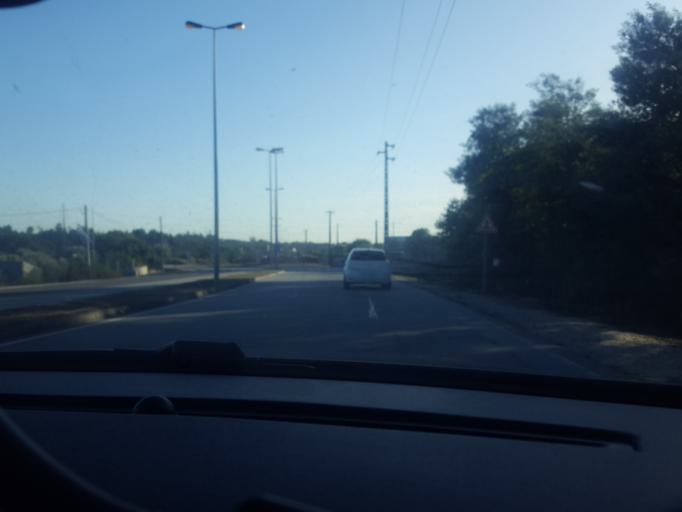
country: PT
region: Viseu
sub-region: Nelas
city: Nelas
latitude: 40.5378
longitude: -7.8585
